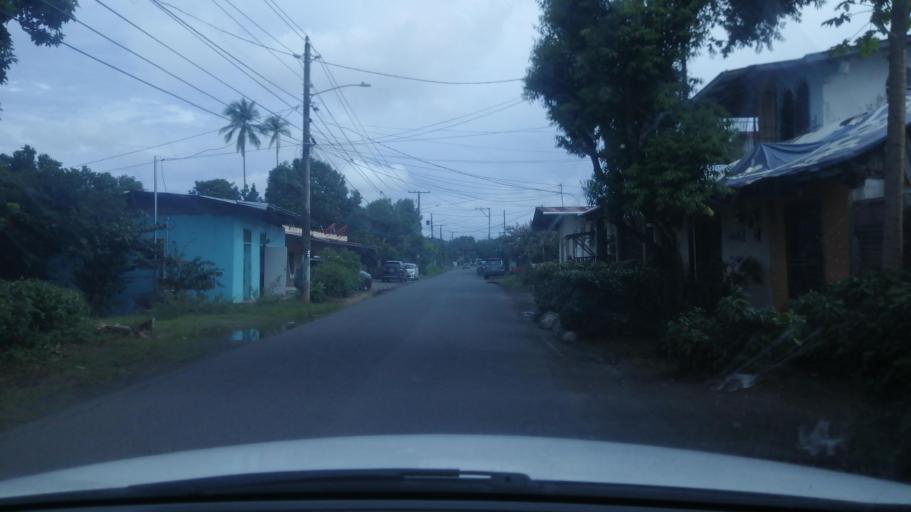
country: PA
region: Chiriqui
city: David
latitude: 8.4239
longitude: -82.4235
